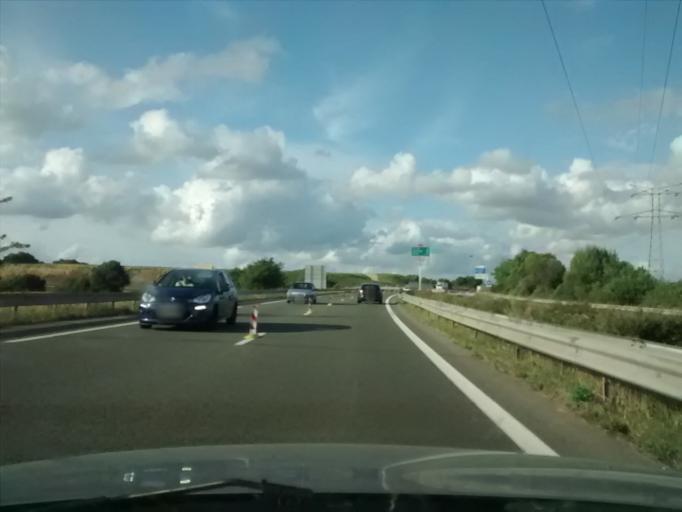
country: FR
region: Pays de la Loire
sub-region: Departement de la Mayenne
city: Saint-Jean-sur-Mayenne
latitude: 48.1061
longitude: -0.7454
